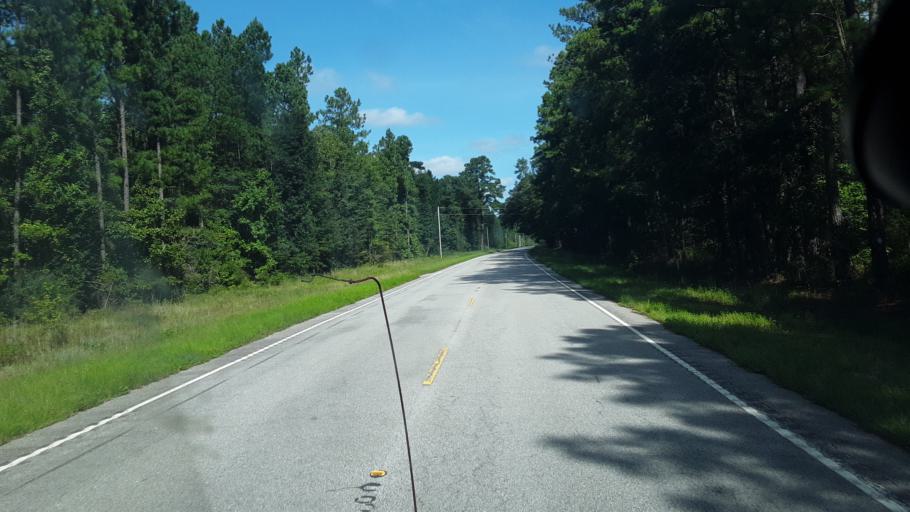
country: US
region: South Carolina
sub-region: Hampton County
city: Varnville
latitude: 32.7399
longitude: -81.0402
